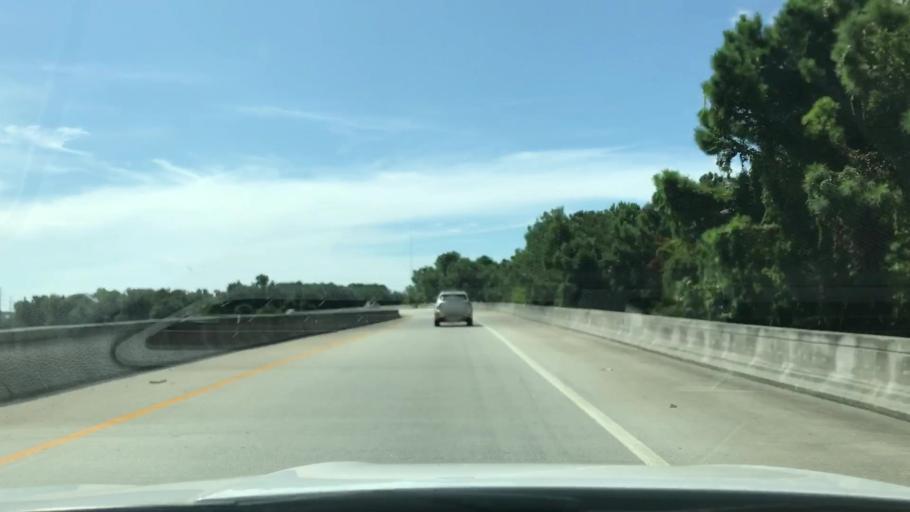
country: US
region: South Carolina
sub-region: Charleston County
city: Mount Pleasant
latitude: 32.8229
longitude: -79.8499
